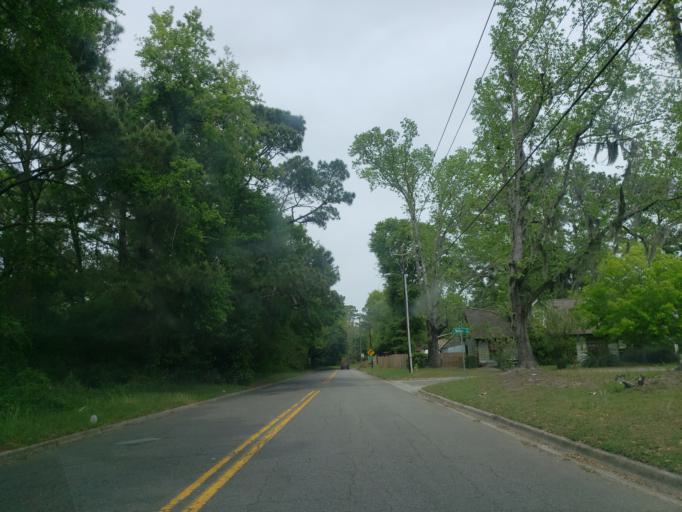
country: US
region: Georgia
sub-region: Chatham County
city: Georgetown
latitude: 31.9904
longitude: -81.1658
